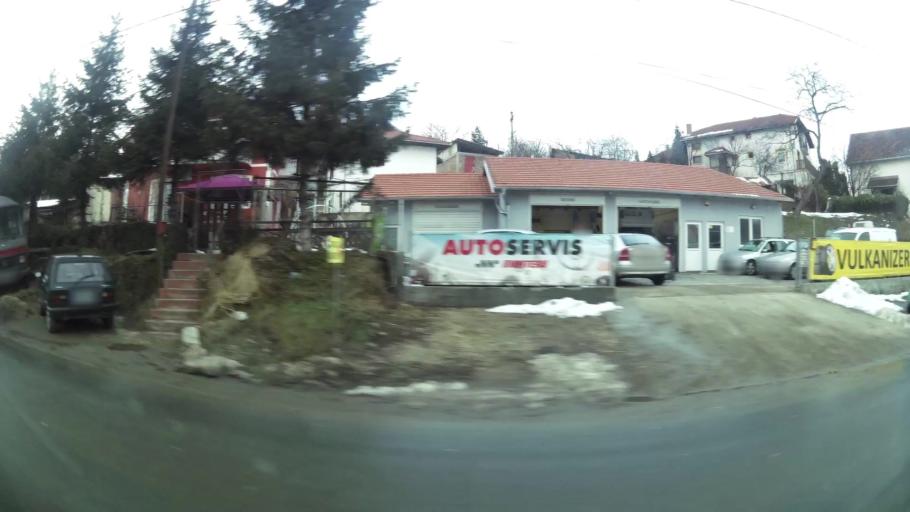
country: RS
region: Central Serbia
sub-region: Belgrade
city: Vozdovac
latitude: 44.7266
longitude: 20.4967
